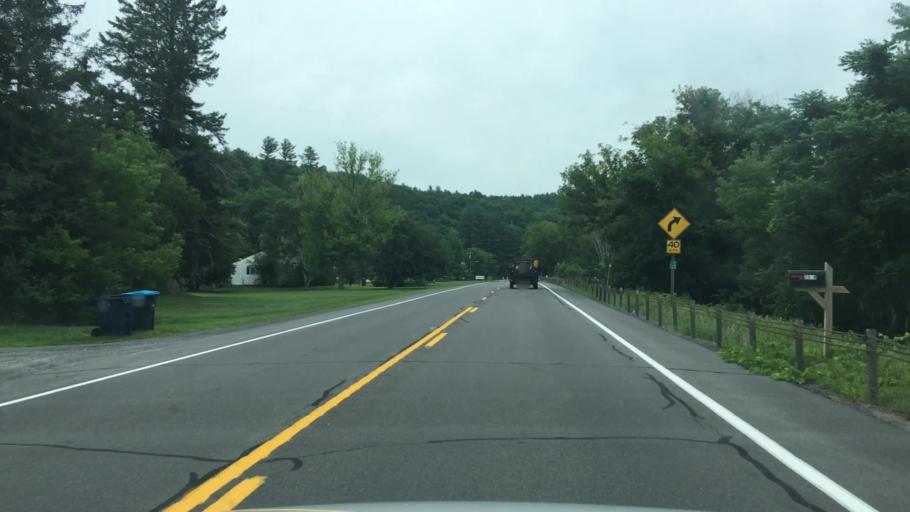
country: US
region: New York
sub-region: Essex County
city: Keeseville
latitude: 44.4562
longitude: -73.6340
